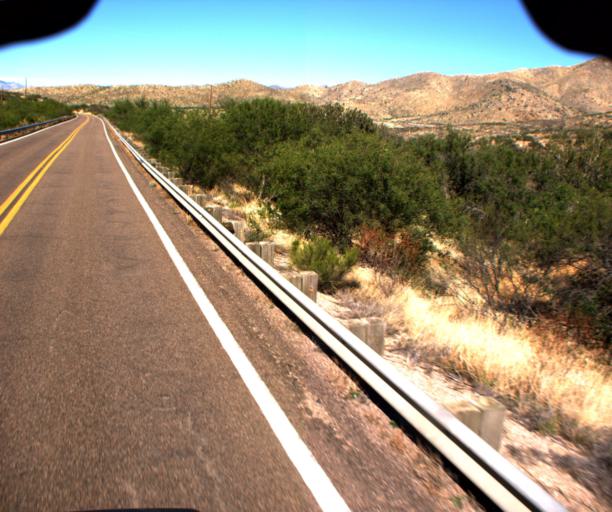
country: US
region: Arizona
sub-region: Pima County
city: Corona de Tucson
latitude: 31.8857
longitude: -110.6724
